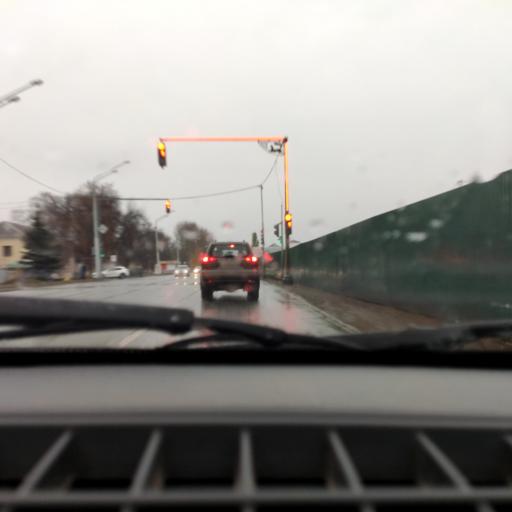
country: RU
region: Bashkortostan
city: Avdon
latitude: 54.6966
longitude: 55.8306
